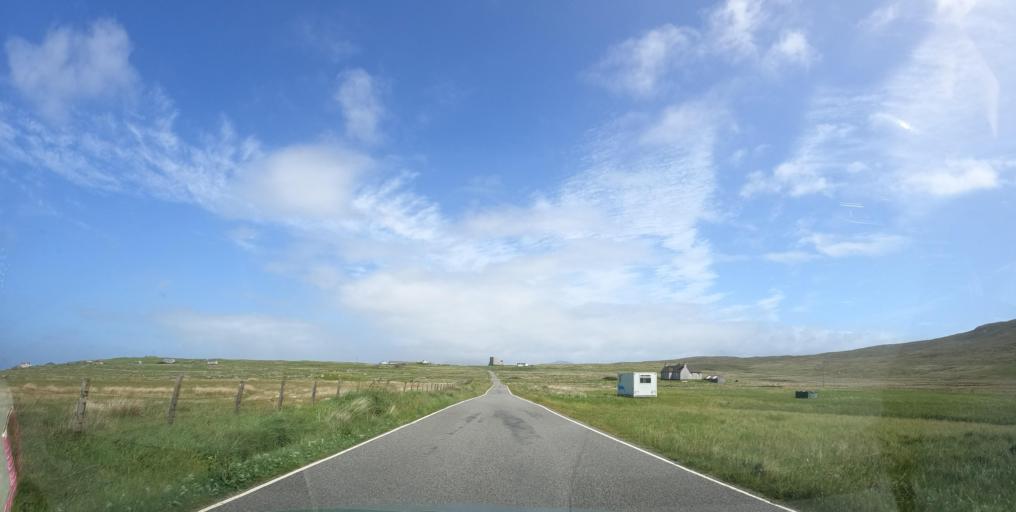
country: GB
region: Scotland
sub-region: Eilean Siar
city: Isle of South Uist
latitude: 57.1188
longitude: -7.3628
